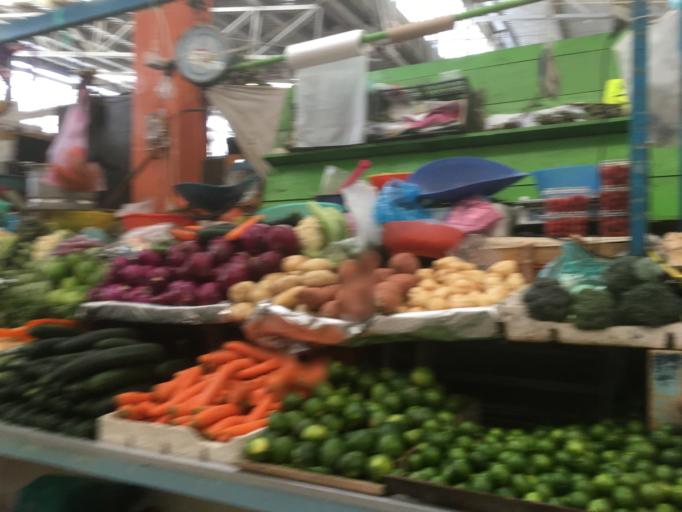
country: MX
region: Mexico City
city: Benito Juarez
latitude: 19.3987
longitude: -99.1438
